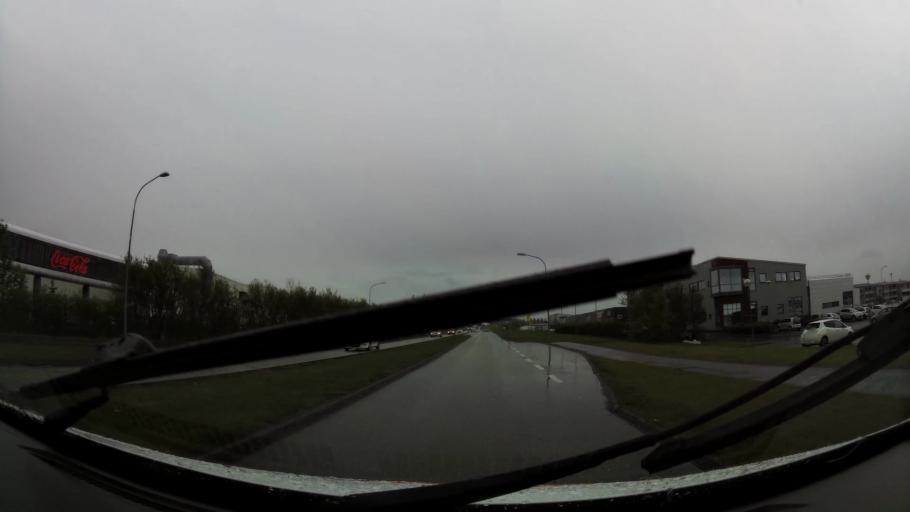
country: IS
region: Capital Region
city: Reykjavik
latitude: 64.1187
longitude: -21.7977
